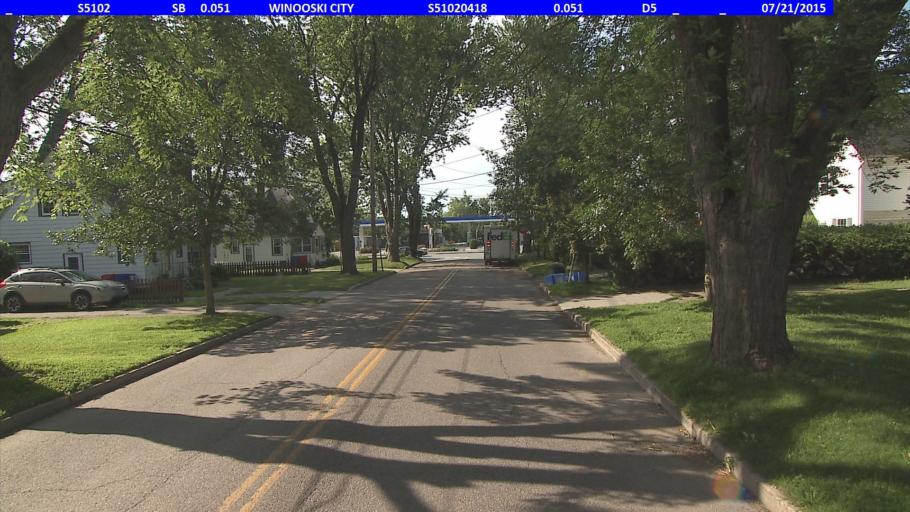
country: US
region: Vermont
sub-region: Chittenden County
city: Winooski
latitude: 44.4938
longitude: -73.1752
